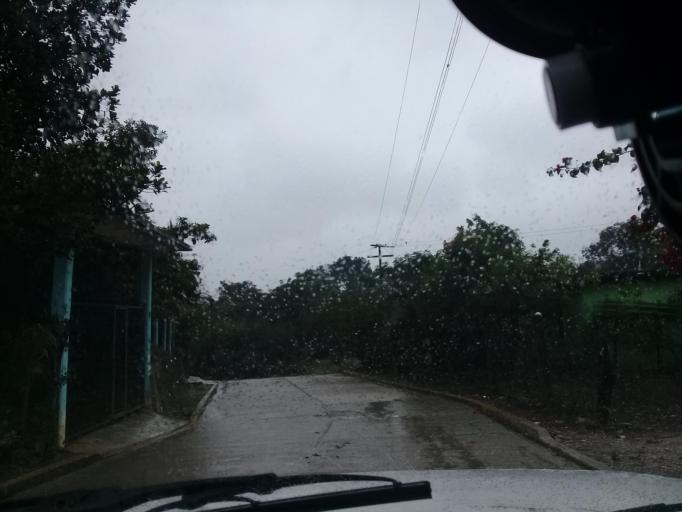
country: MX
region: Veracruz
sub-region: Chalma
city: San Pedro Coyutla
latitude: 21.1813
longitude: -98.4345
